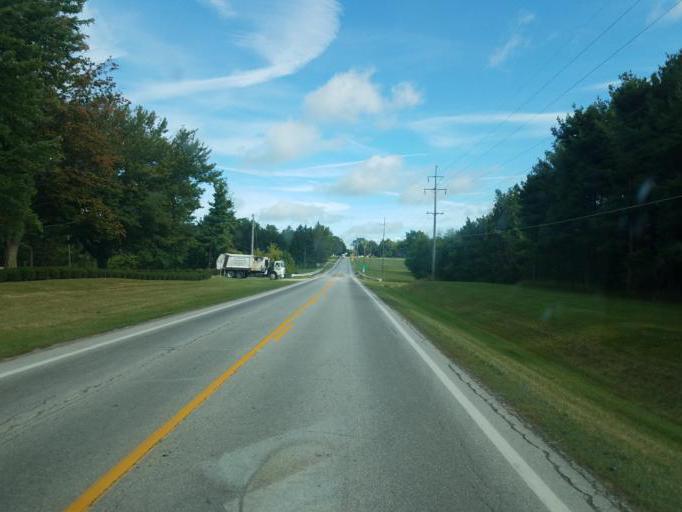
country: US
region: Ohio
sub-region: Wayne County
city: West Salem
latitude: 41.0897
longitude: -82.1235
